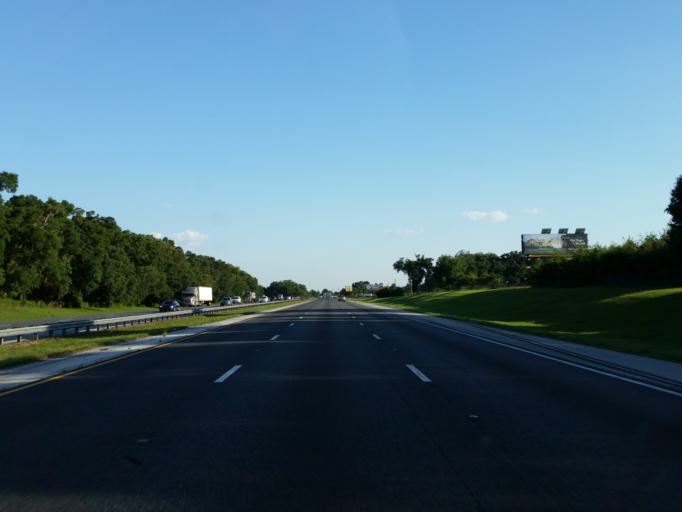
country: US
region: Florida
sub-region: Marion County
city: Ocala
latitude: 29.2411
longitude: -82.1901
